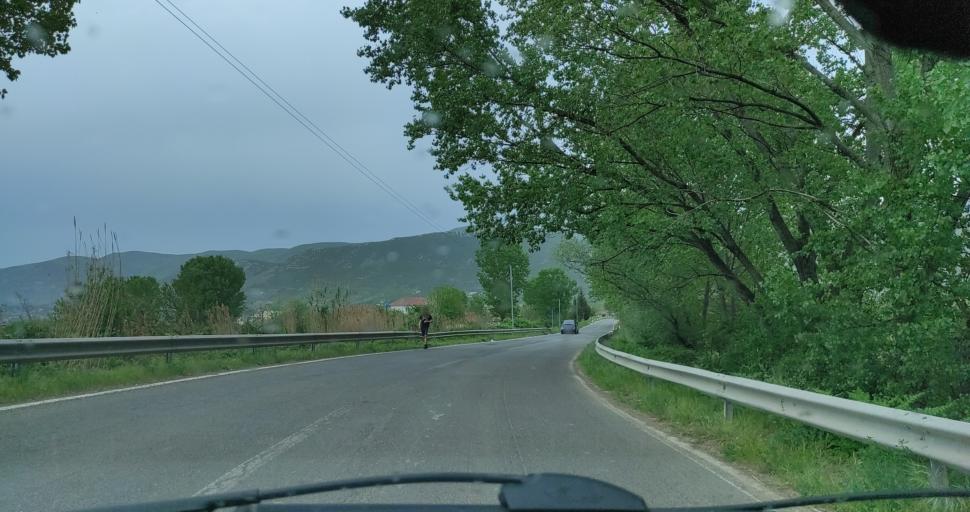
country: AL
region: Lezhe
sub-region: Rrethi i Kurbinit
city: Mamurras
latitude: 41.6005
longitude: 19.7000
